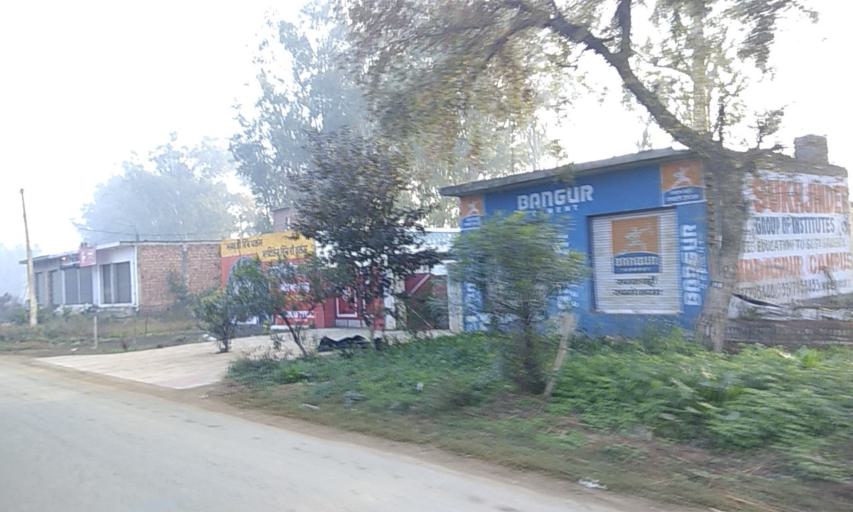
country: IN
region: Punjab
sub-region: Gurdaspur
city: Dhariwal
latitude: 31.9386
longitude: 75.3099
